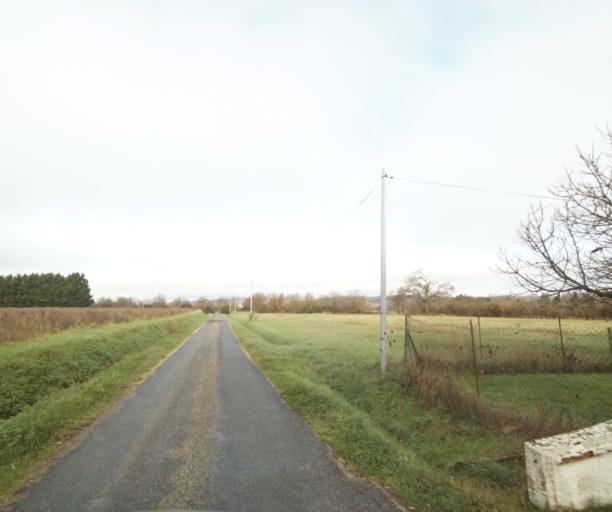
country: FR
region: Midi-Pyrenees
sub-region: Departement de la Haute-Garonne
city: Villemur-sur-Tarn
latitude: 43.8731
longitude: 1.4804
